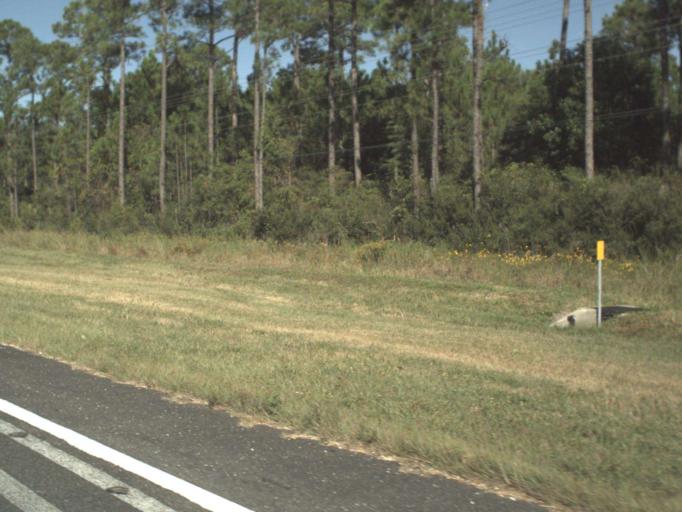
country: US
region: Florida
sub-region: Walton County
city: Seaside
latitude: 30.3669
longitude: -86.1851
